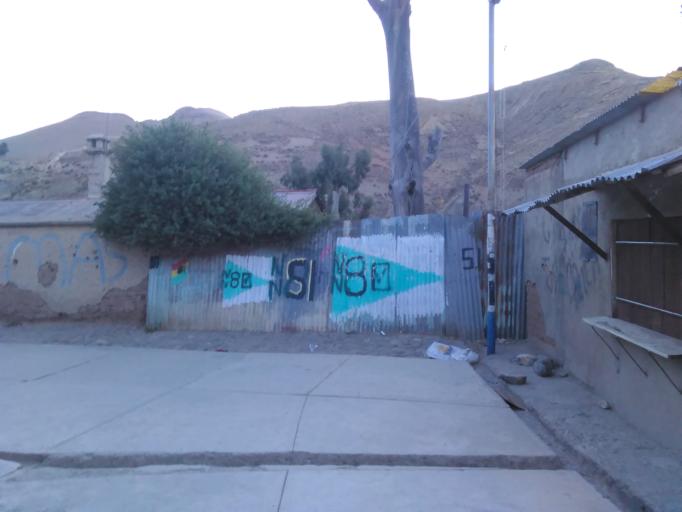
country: BO
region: Potosi
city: Llallagua
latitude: -18.4240
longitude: -66.5923
